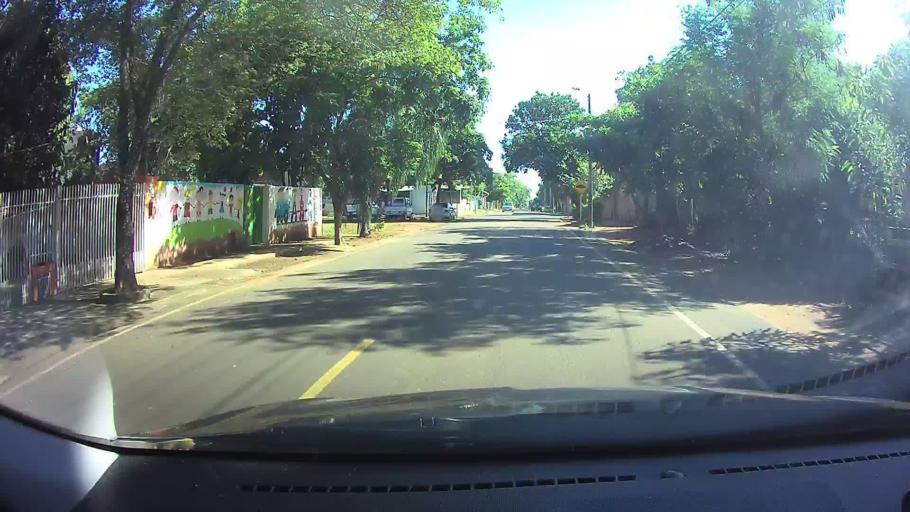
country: PY
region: Central
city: San Lorenzo
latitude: -25.2781
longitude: -57.5057
